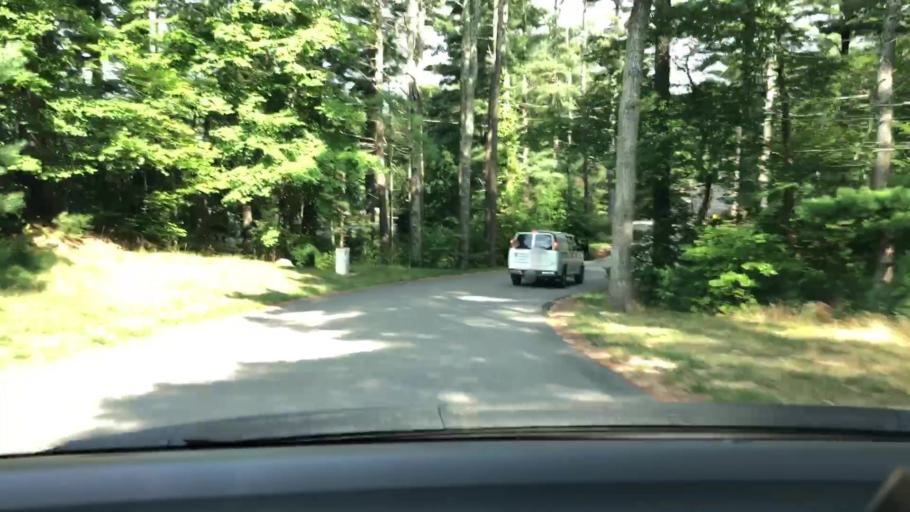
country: US
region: Massachusetts
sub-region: Plymouth County
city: White Island Shores
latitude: 41.8922
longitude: -70.5861
